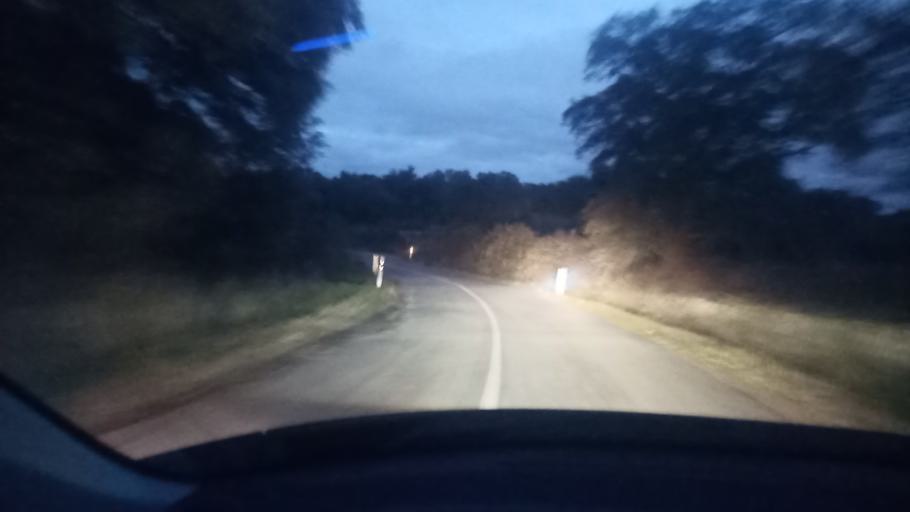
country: ES
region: Madrid
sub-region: Provincia de Madrid
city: Colmenar del Arroyo
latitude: 40.4313
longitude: -4.2239
